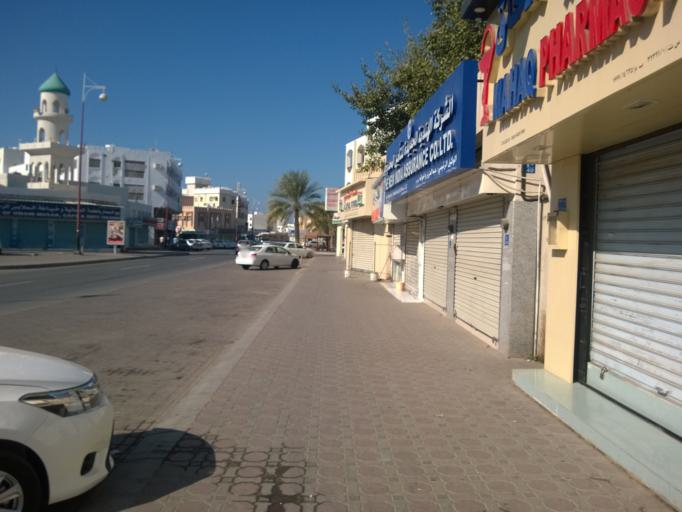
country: OM
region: Muhafazat Masqat
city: As Sib al Jadidah
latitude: 23.6807
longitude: 58.1869
